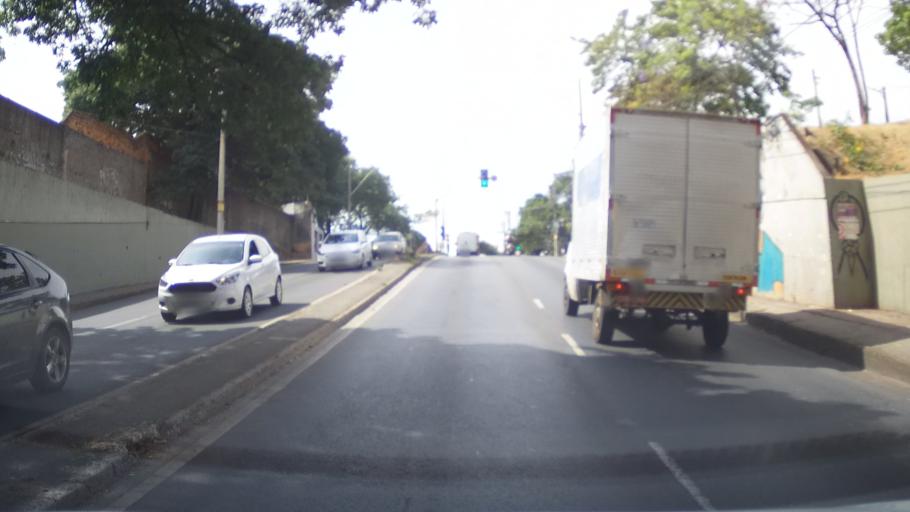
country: BR
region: Minas Gerais
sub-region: Belo Horizonte
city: Belo Horizonte
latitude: -19.9270
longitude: -43.9870
